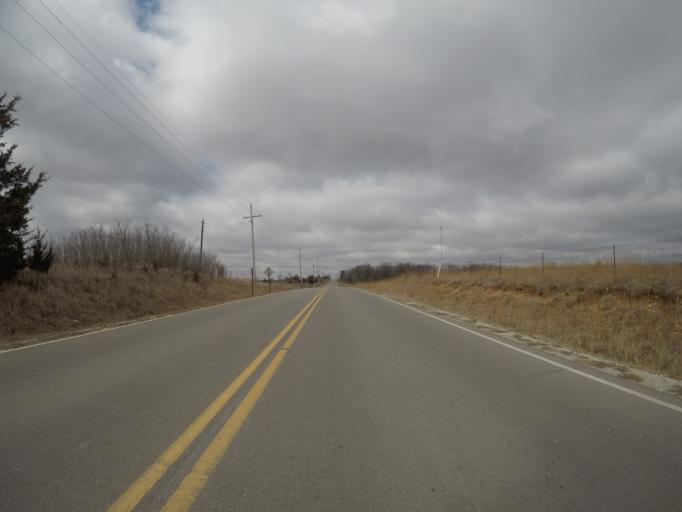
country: US
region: Kansas
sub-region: Pottawatomie County
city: Westmoreland
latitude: 39.3993
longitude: -96.4189
